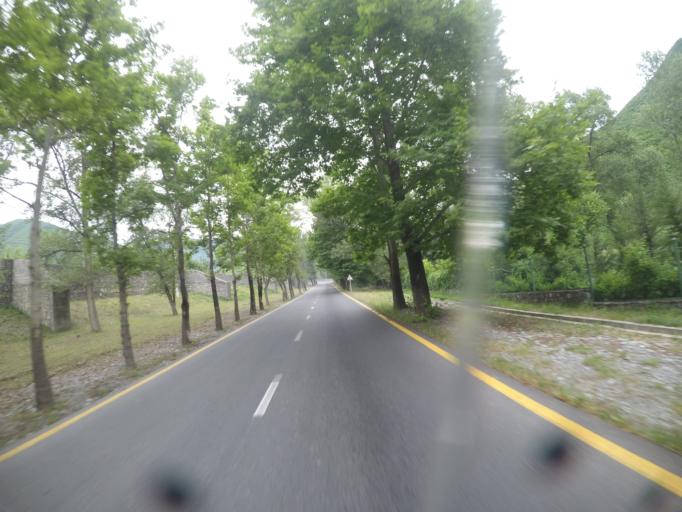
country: AZ
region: Shaki City
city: Sheki
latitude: 41.2398
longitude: 47.1849
